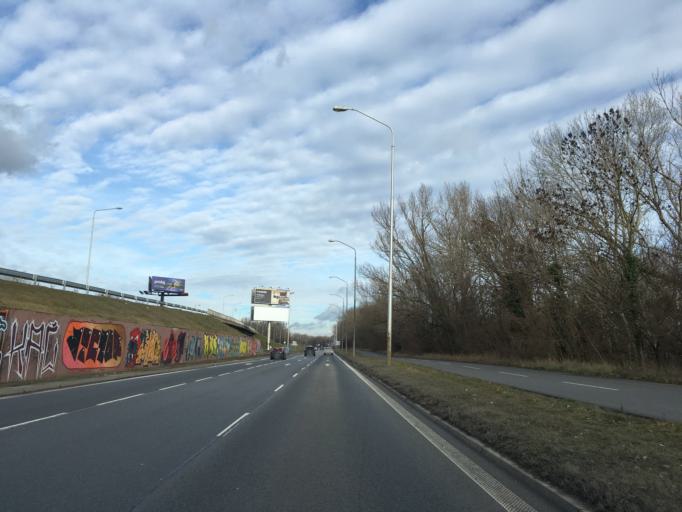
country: SK
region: Bratislavsky
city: Bratislava
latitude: 48.1108
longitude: 17.1277
